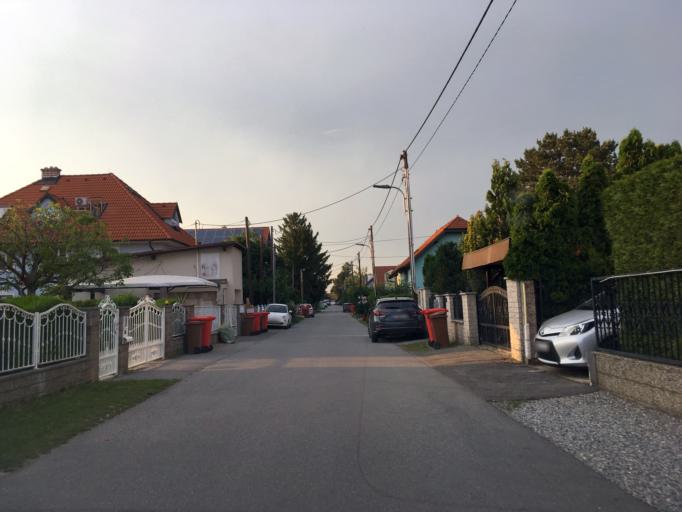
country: AT
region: Lower Austria
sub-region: Politischer Bezirk Wien-Umgebung
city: Gerasdorf bei Wien
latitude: 48.3118
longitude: 16.4999
